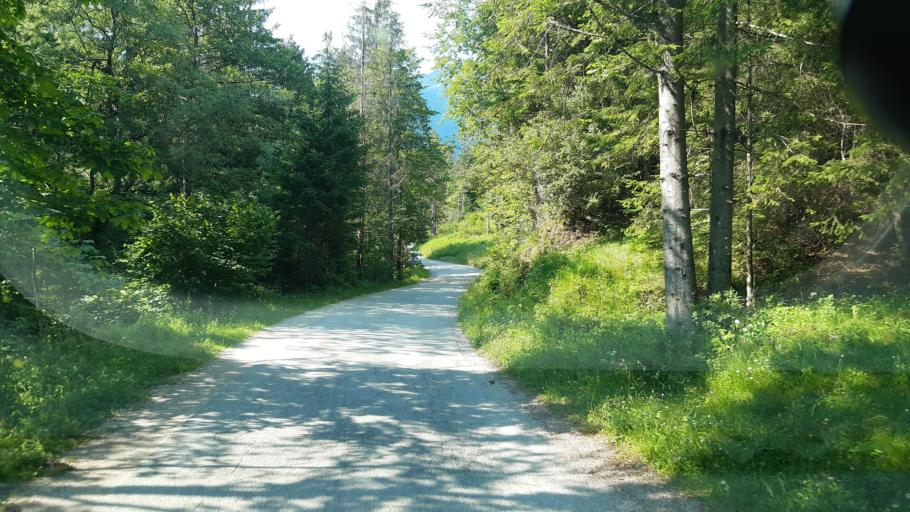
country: SI
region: Radovljica
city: Radovljica
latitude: 46.3823
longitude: 14.2181
